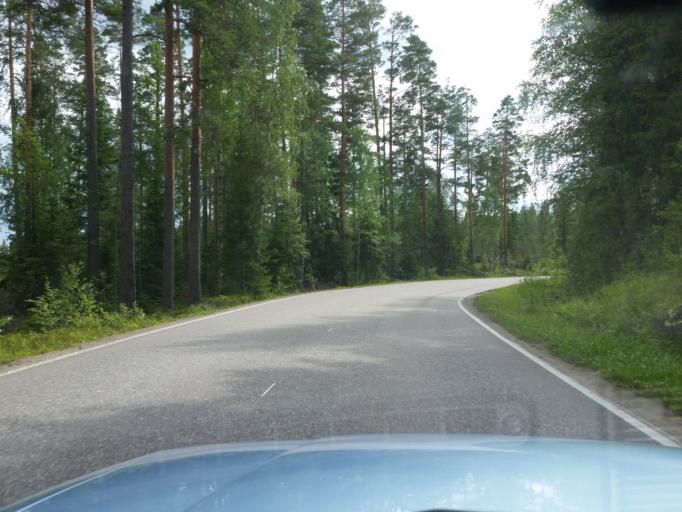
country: FI
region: Southern Savonia
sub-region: Savonlinna
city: Sulkava
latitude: 61.7975
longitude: 28.4116
